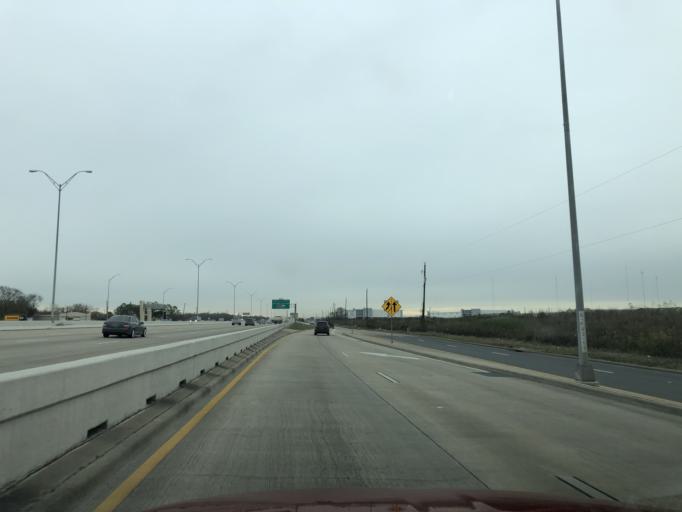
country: US
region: Texas
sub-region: Fort Bend County
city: Missouri City
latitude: 29.6346
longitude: -95.5274
